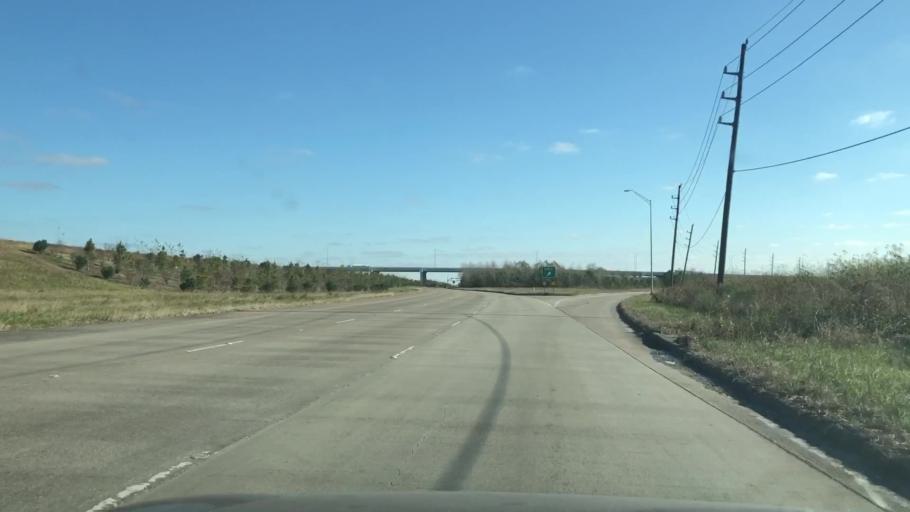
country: US
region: Texas
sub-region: Harris County
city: Cloverleaf
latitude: 29.8294
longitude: -95.1813
